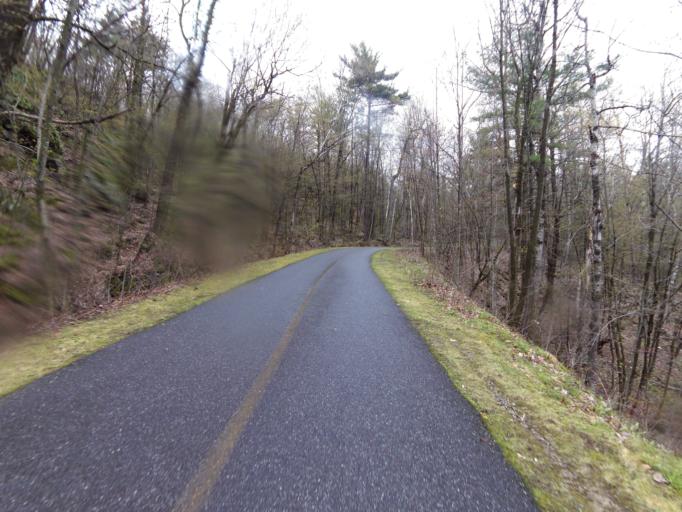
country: CA
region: Quebec
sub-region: Outaouais
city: Gatineau
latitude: 45.4542
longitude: -75.7731
